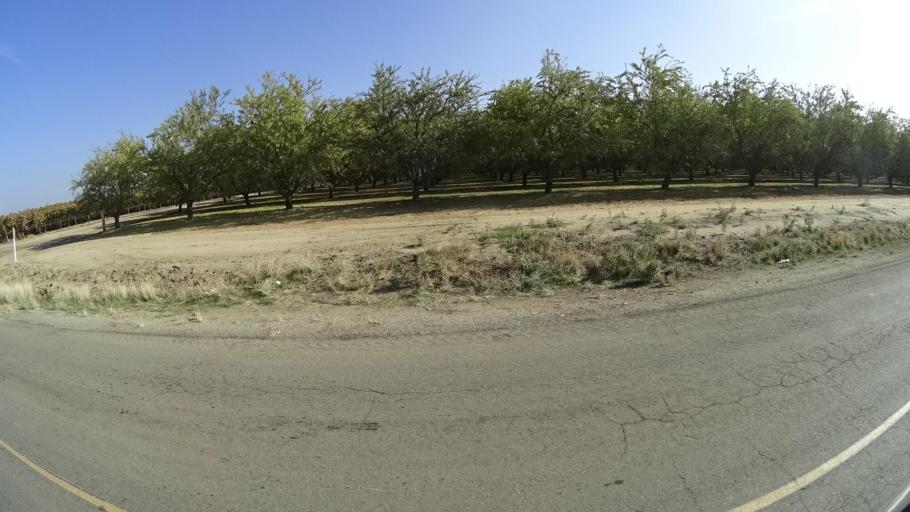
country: US
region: California
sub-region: Kern County
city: McFarland
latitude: 35.6455
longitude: -119.1691
